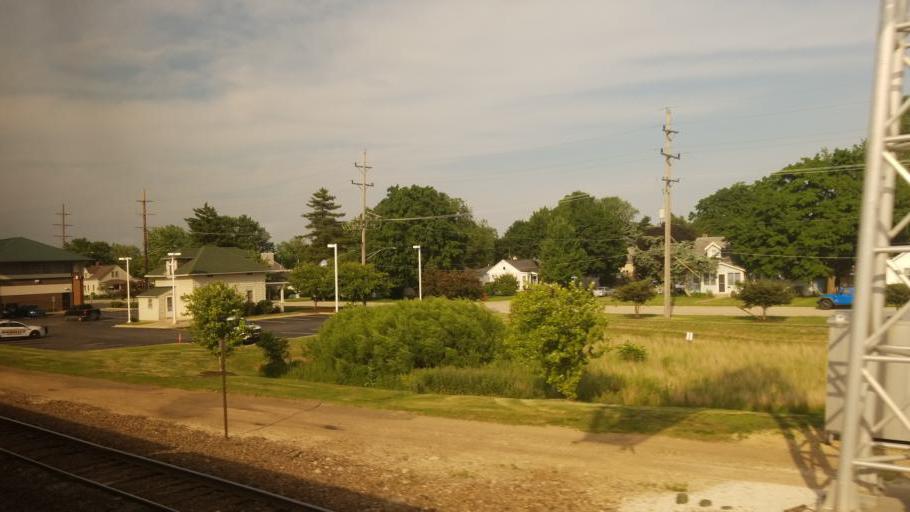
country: US
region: Illinois
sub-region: Kane County
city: Montgomery
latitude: 41.7279
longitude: -88.3464
